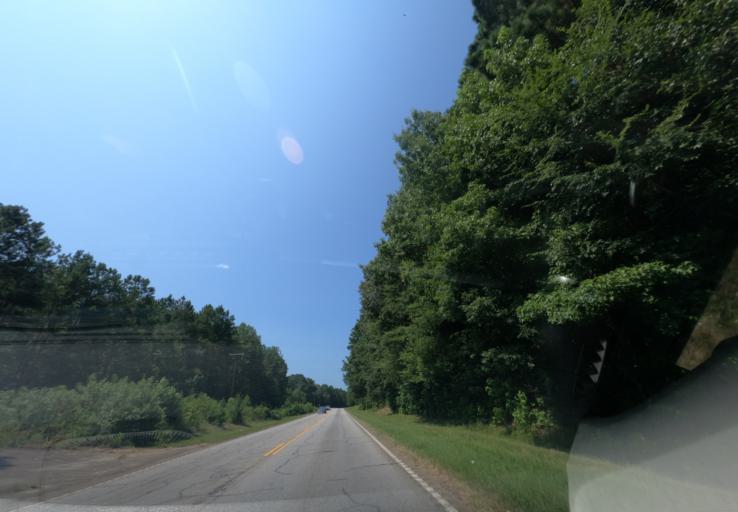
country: US
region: South Carolina
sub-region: Greenwood County
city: Greenwood
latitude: 34.1602
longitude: -82.1298
